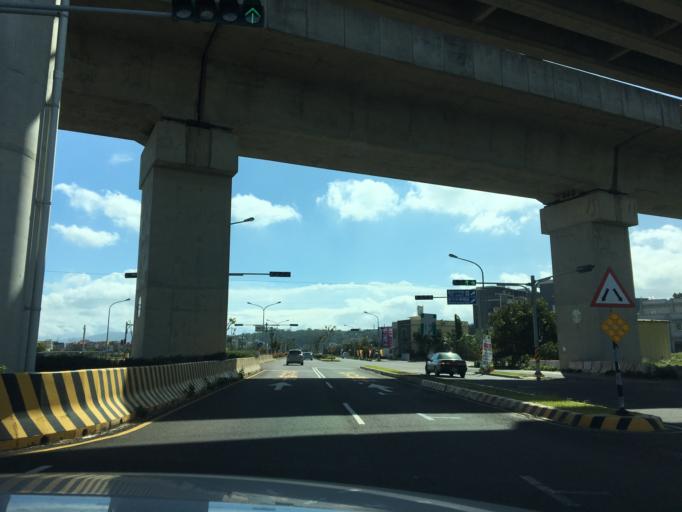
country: TW
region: Taiwan
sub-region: Hsinchu
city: Zhubei
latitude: 24.7855
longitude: 121.0345
